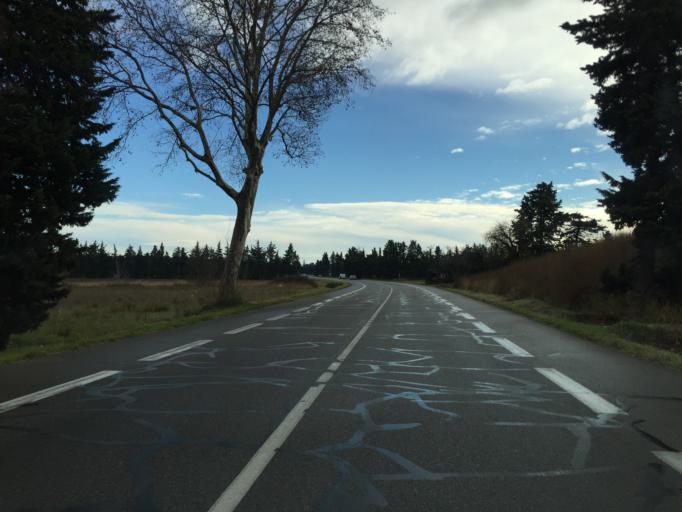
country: FR
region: Provence-Alpes-Cote d'Azur
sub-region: Departement du Vaucluse
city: Velleron
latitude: 43.9696
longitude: 5.0210
